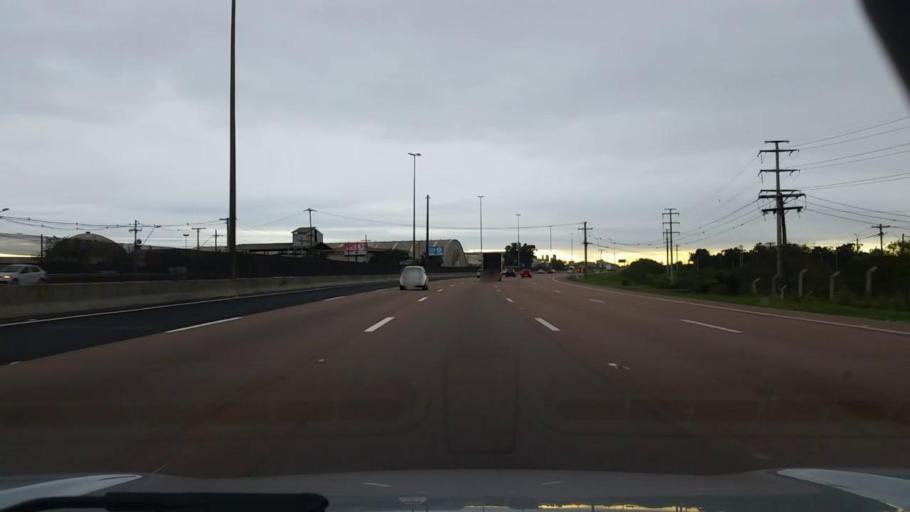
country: BR
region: Rio Grande do Sul
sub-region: Canoas
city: Canoas
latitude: -29.9718
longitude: -51.1947
